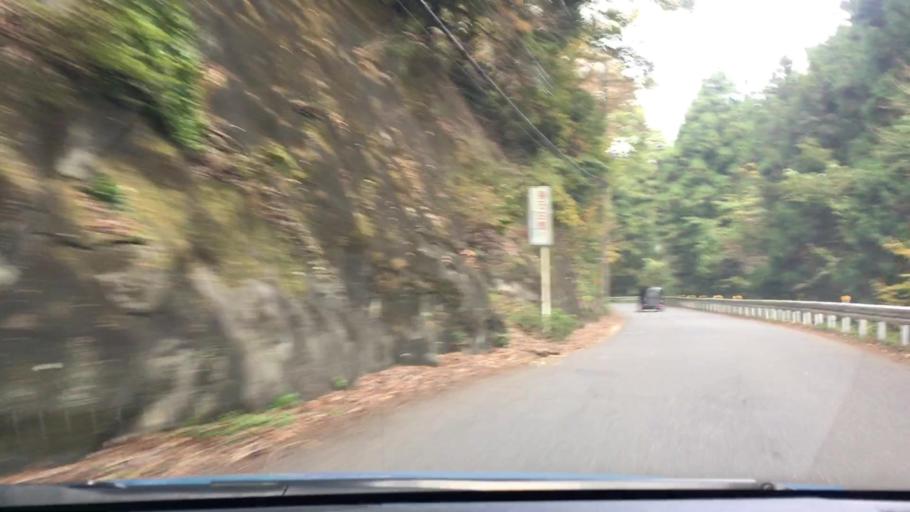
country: JP
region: Yamanashi
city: Uenohara
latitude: 35.5599
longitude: 139.1423
